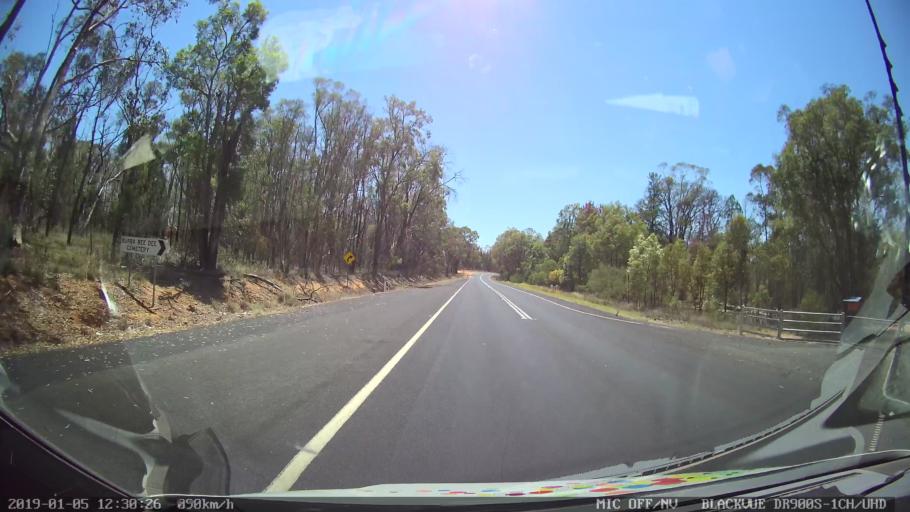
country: AU
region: New South Wales
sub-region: Warrumbungle Shire
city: Coonabarabran
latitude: -31.2278
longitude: 149.3503
